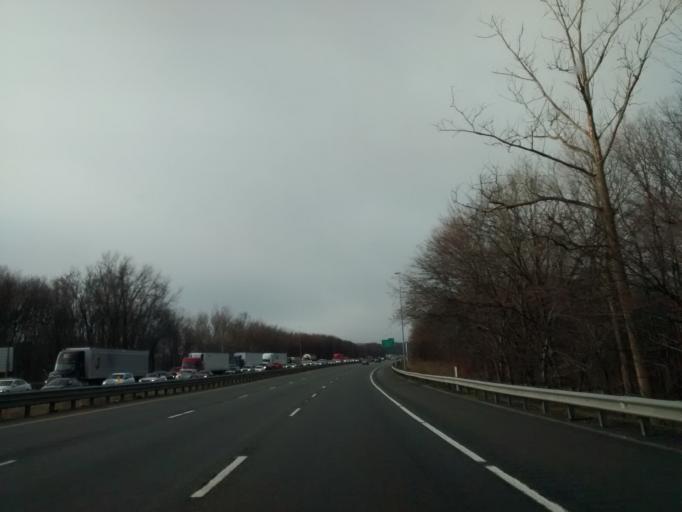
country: US
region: Massachusetts
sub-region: Worcester County
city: Auburn
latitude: 42.2194
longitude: -71.8290
